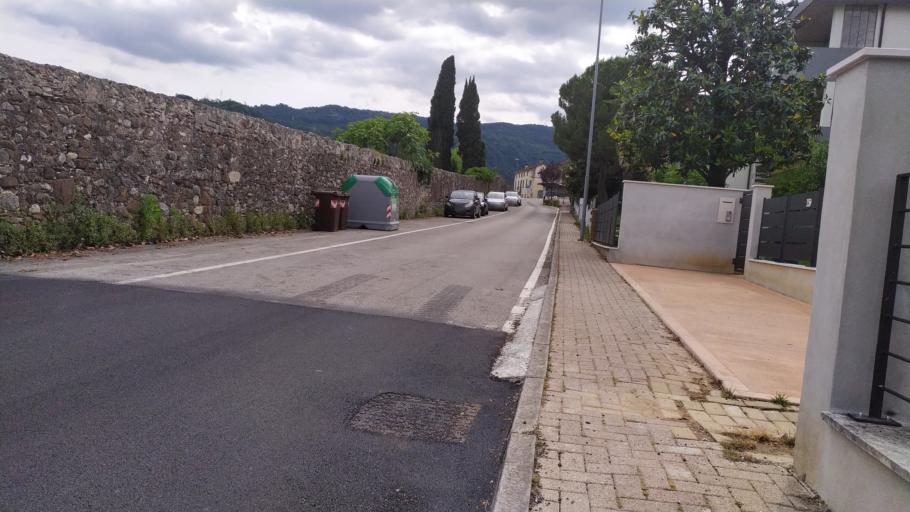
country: IT
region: Veneto
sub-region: Provincia di Vicenza
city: Schio
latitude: 45.7032
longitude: 11.3438
